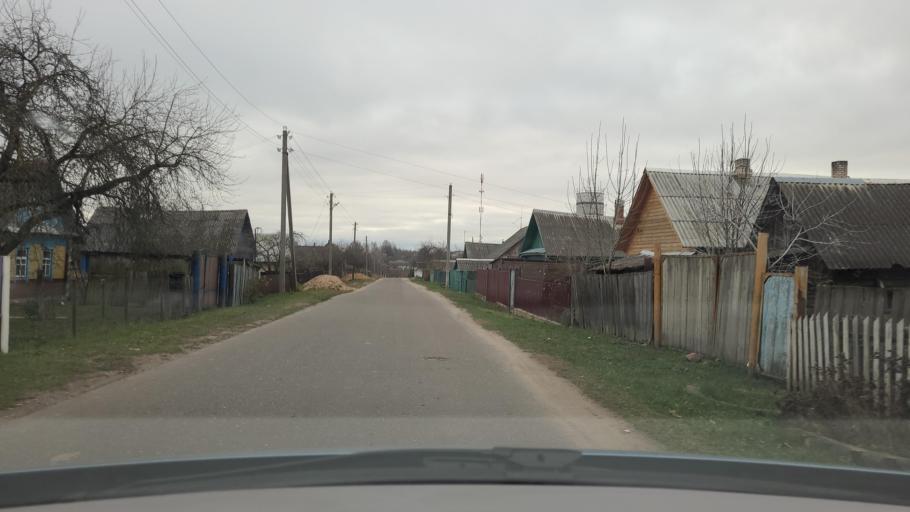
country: BY
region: Minsk
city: Khalopyenichy
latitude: 54.5171
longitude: 28.9550
